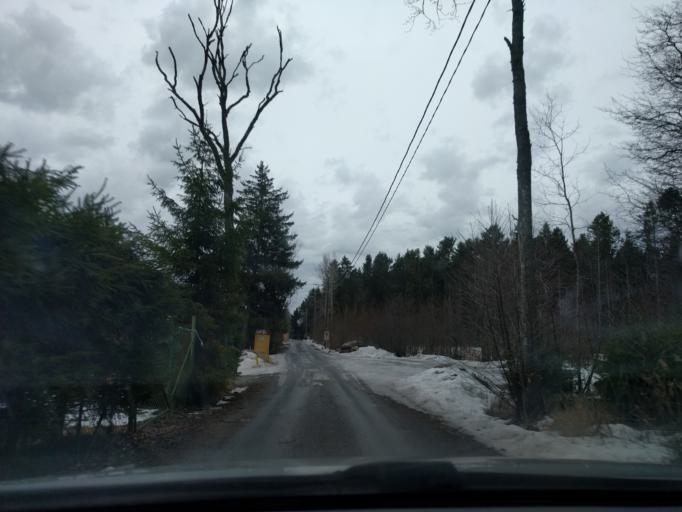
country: EE
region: Harju
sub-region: Viimsi vald
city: Viimsi
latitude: 59.5153
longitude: 24.9055
